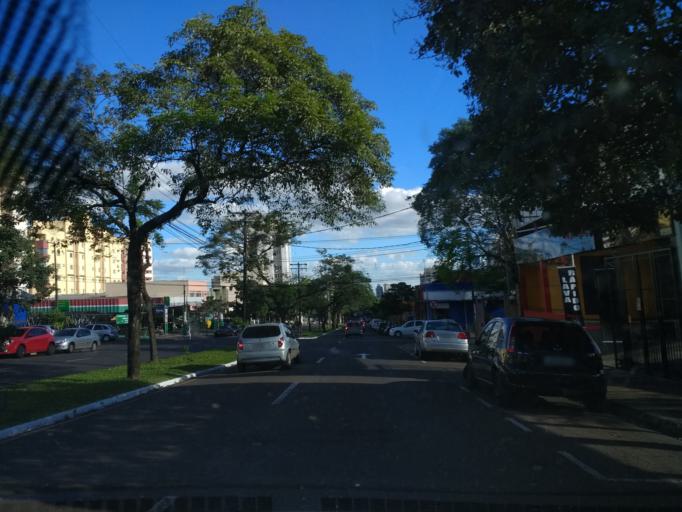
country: BR
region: Parana
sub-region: Londrina
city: Londrina
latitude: -23.3227
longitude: -51.1551
